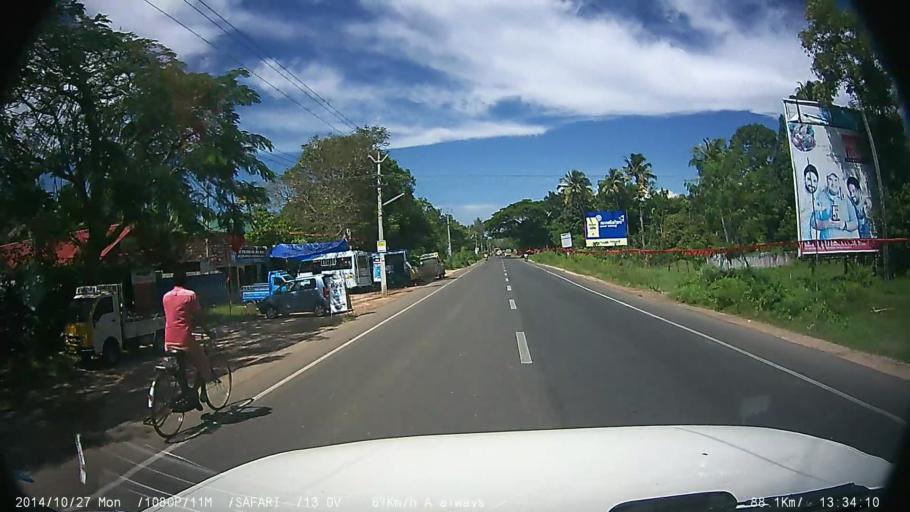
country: IN
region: Kerala
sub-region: Alappuzha
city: Alleppey
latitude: 9.5815
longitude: 76.3275
